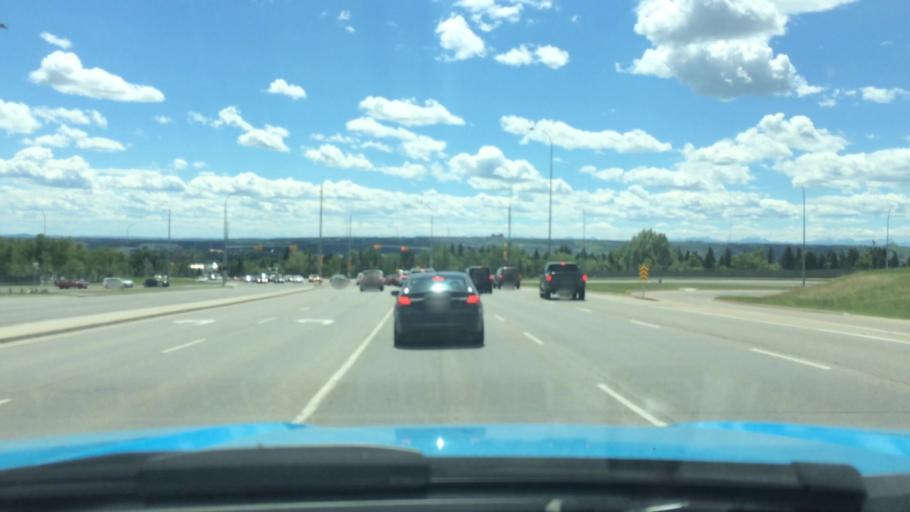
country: CA
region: Alberta
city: Calgary
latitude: 51.1104
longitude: -114.1393
